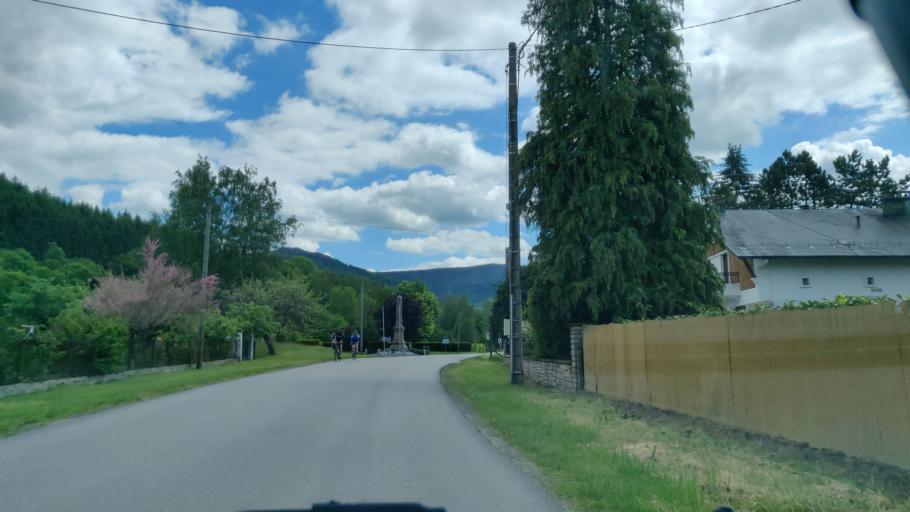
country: FR
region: Lorraine
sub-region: Departement des Vosges
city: Fraize
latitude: 48.1693
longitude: 6.9809
